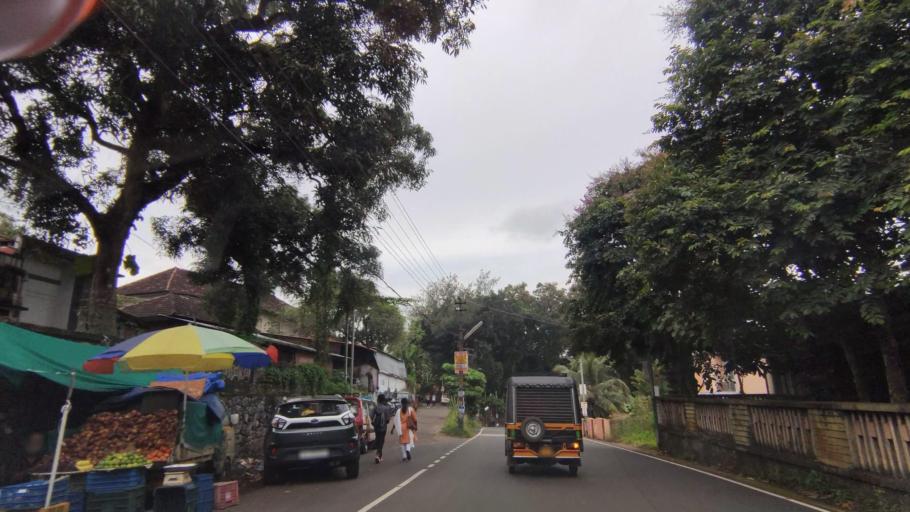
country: IN
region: Kerala
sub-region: Kottayam
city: Kottayam
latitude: 9.5965
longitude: 76.5163
